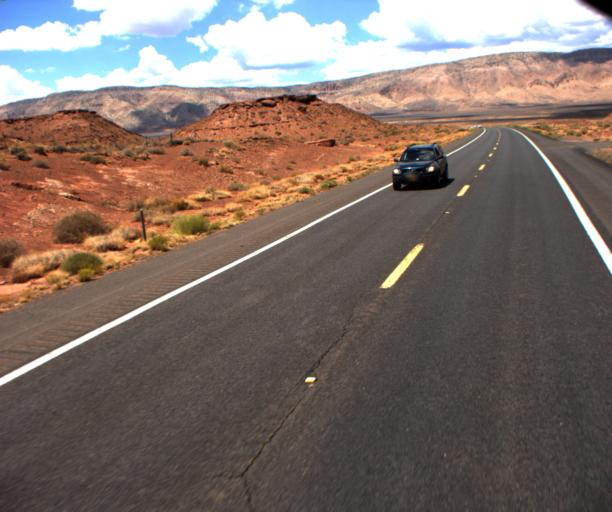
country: US
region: Arizona
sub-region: Coconino County
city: Tuba City
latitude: 35.8731
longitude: -111.5033
